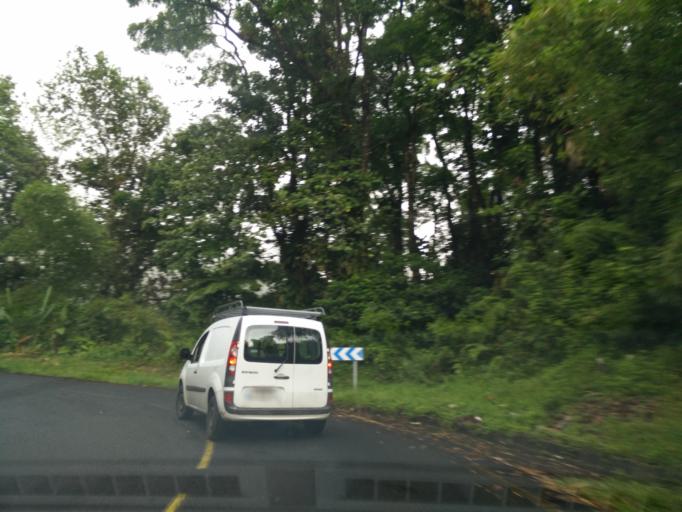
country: MQ
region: Martinique
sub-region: Martinique
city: Le Morne-Rouge
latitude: 14.7248
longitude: -61.1022
